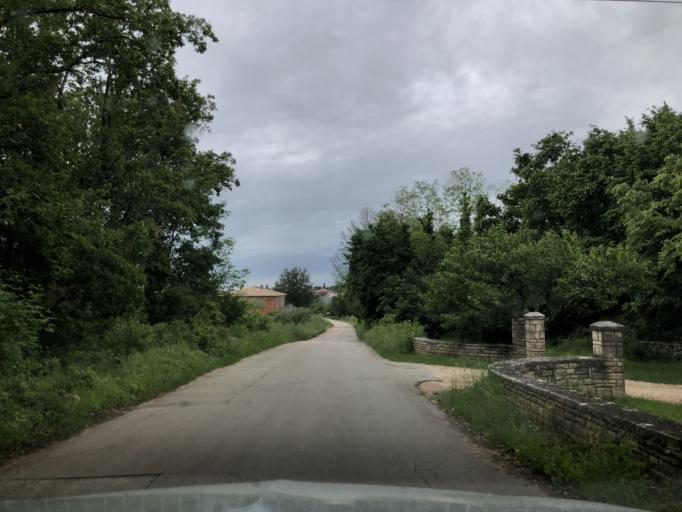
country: HR
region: Istarska
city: Buje
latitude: 45.4391
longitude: 13.6613
